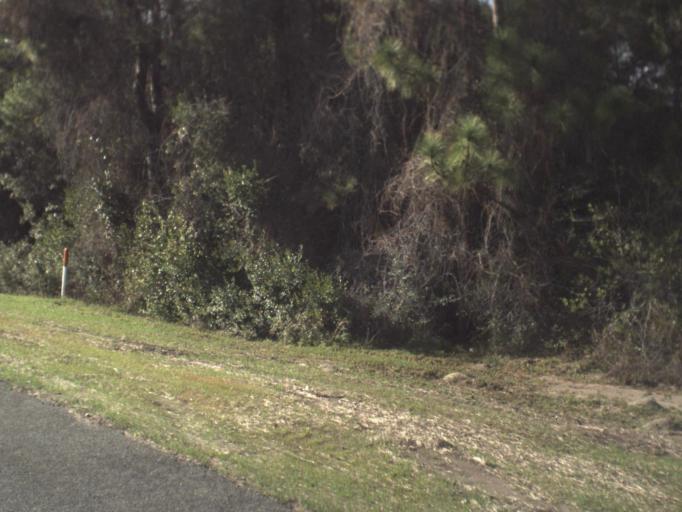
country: US
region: Florida
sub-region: Bay County
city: Youngstown
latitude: 30.4357
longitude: -85.4374
